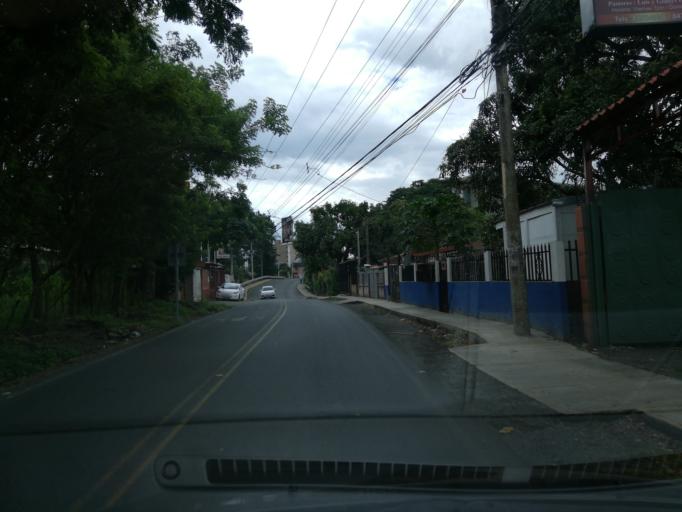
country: CR
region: Alajuela
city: Alajuela
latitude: 10.0027
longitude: -84.2103
